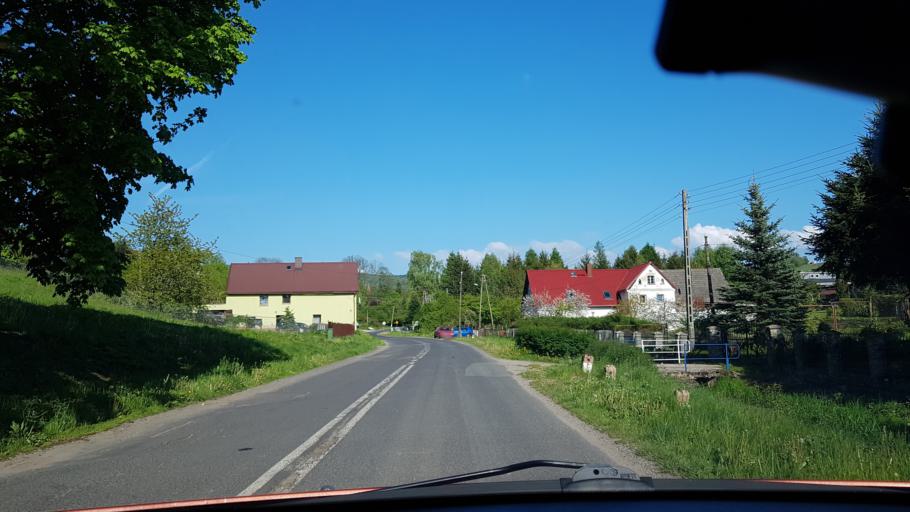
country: PL
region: Lower Silesian Voivodeship
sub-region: Powiat klodzki
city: Nowa Ruda
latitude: 50.5896
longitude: 16.5459
